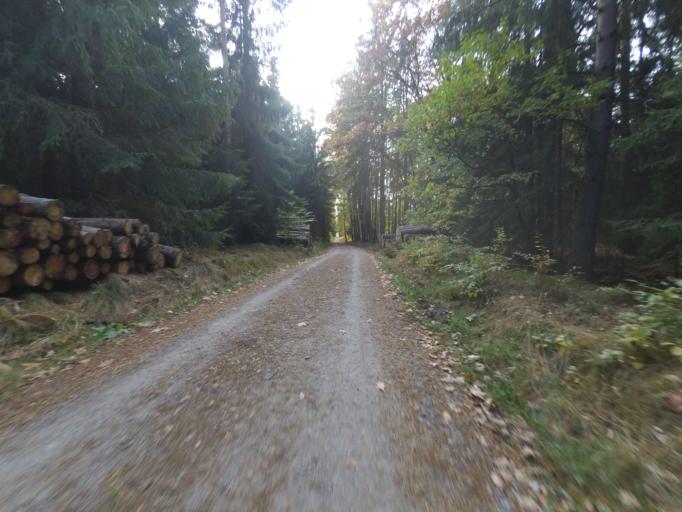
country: DE
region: Saxony
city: Radeberg
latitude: 51.0852
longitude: 13.8594
